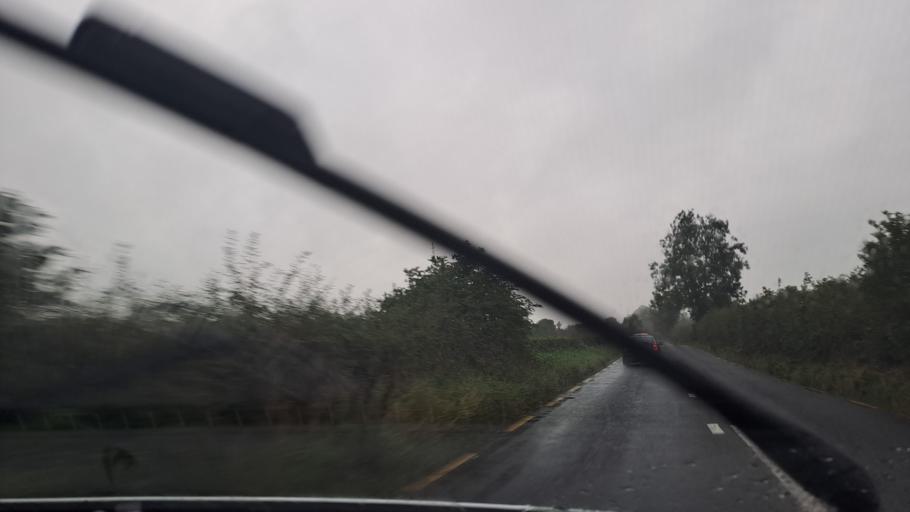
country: IE
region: Leinster
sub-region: Lu
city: Dundalk
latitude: 53.9886
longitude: -6.4802
